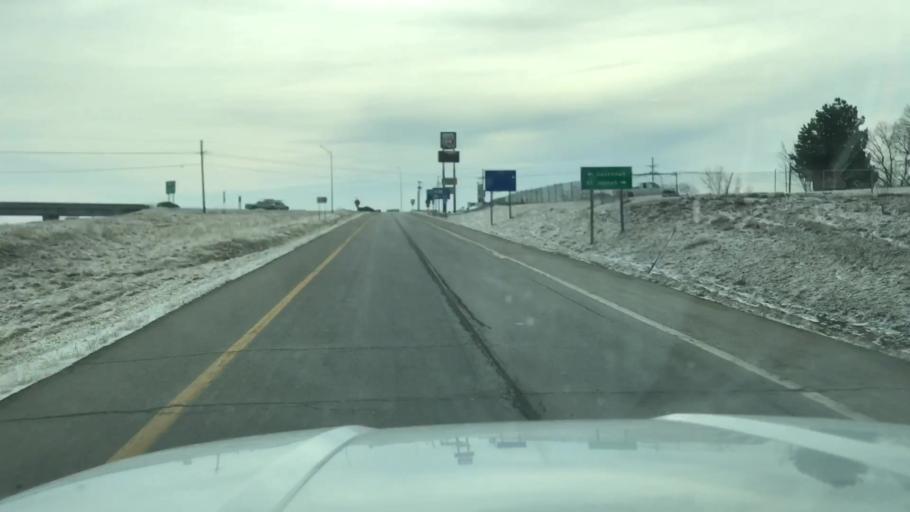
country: US
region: Missouri
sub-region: Andrew County
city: Country Club Village
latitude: 39.8587
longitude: -94.8127
